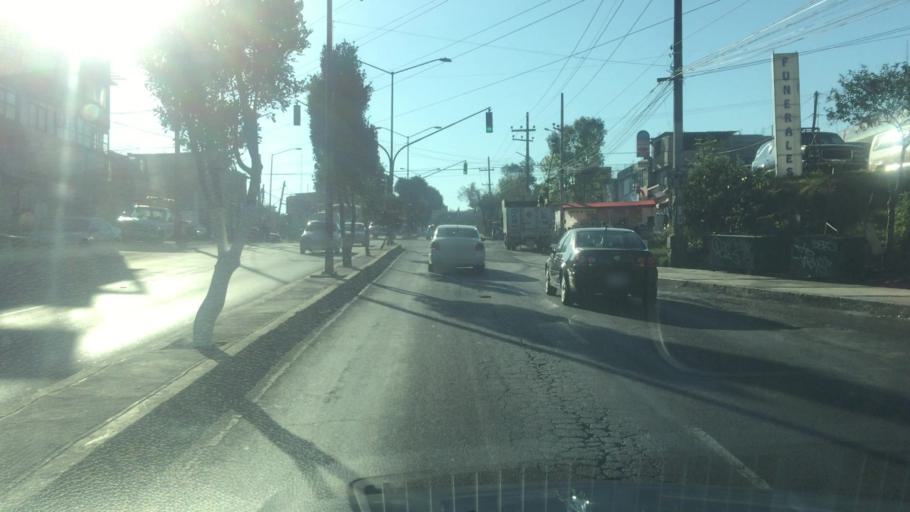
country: MX
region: Mexico City
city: Tlalpan
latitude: 19.2744
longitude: -99.2073
